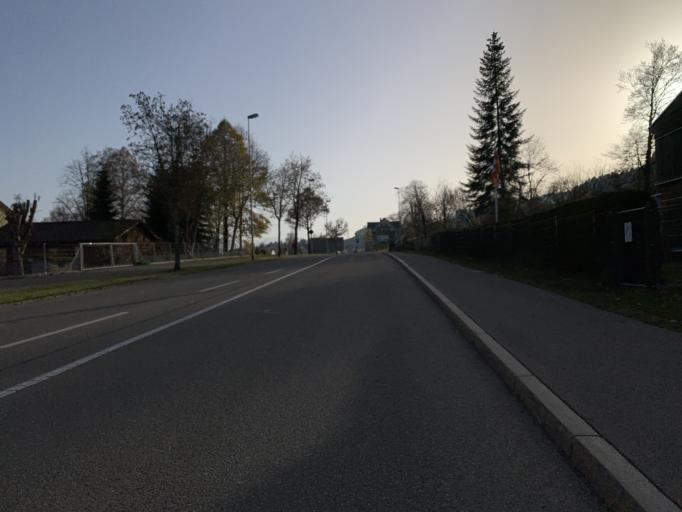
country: CH
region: Zurich
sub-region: Bezirk Hinwil
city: Wald
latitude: 47.3120
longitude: 8.9135
